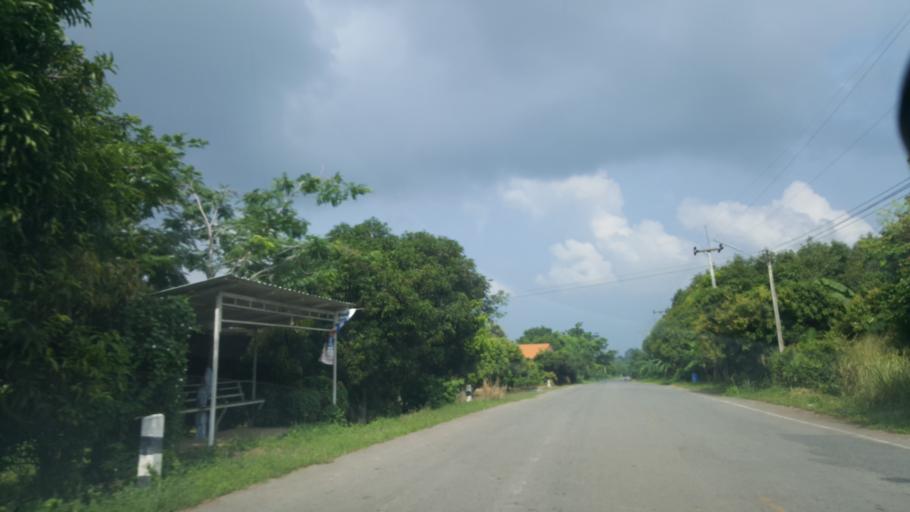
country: TH
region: Chon Buri
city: Sattahip
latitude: 12.7164
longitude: 100.9200
